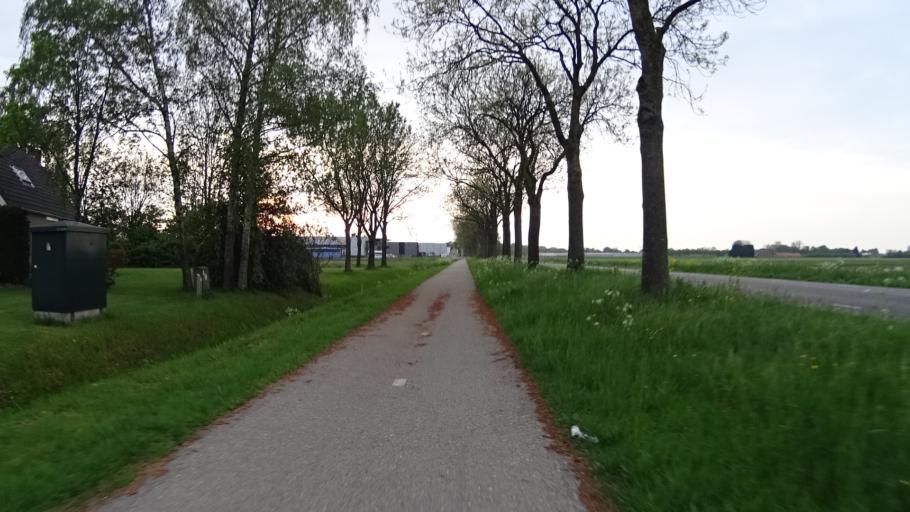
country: NL
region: North Brabant
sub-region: Gemeente Woudrichem
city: Woudrichem
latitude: 51.7802
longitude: 5.0439
